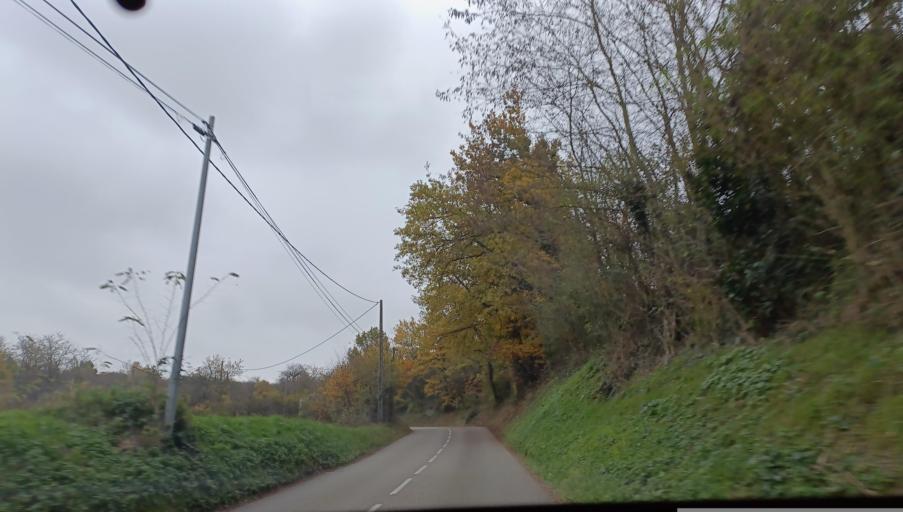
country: FR
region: Rhone-Alpes
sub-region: Departement de l'Isere
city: Serpaize
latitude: 45.5478
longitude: 4.9218
